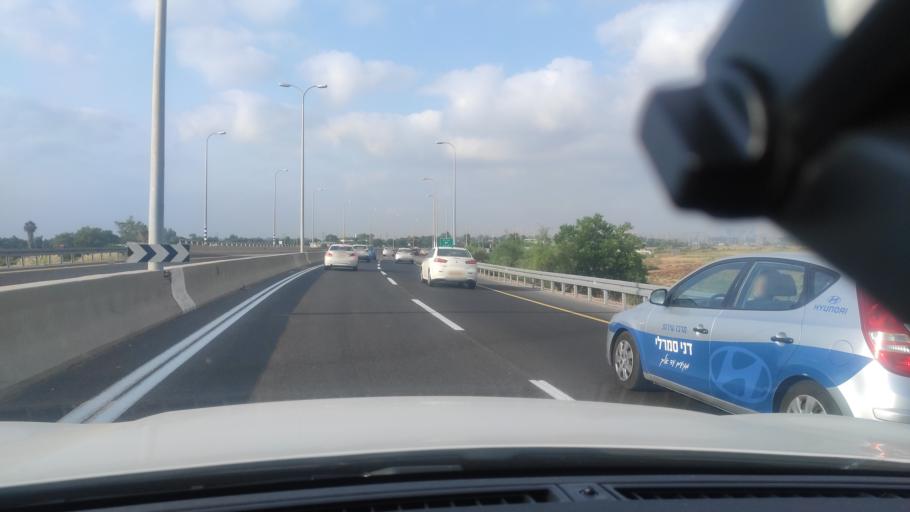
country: IL
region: Central District
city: Hod HaSharon
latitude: 32.1415
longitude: 34.9176
